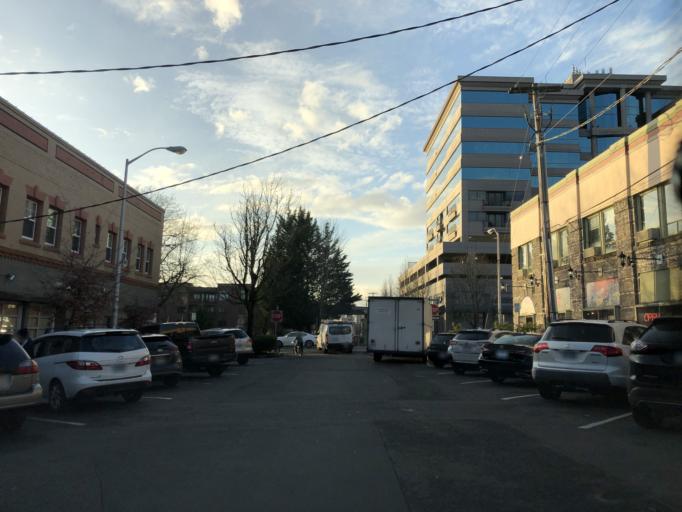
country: US
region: Washington
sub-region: Clark County
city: Vancouver
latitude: 45.6280
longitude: -122.6720
